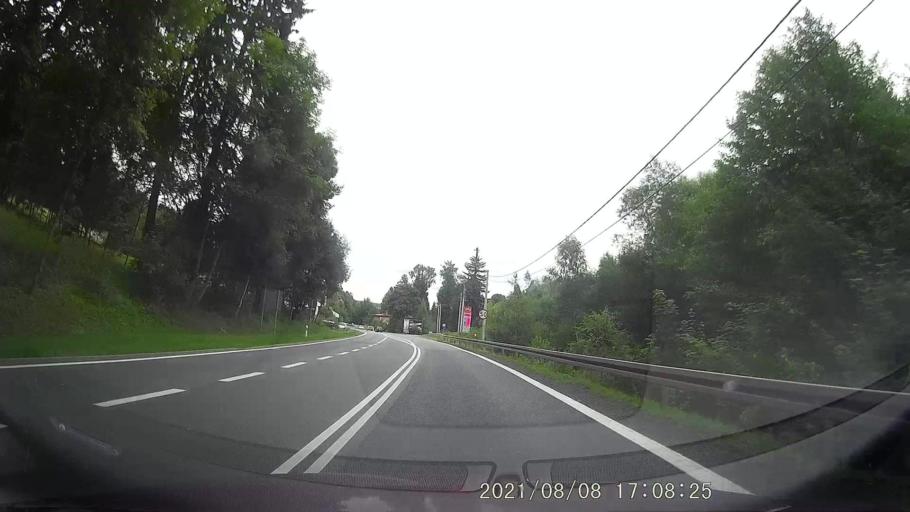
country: PL
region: Lower Silesian Voivodeship
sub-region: Powiat klodzki
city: Duszniki-Zdroj
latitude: 50.3930
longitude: 16.3665
